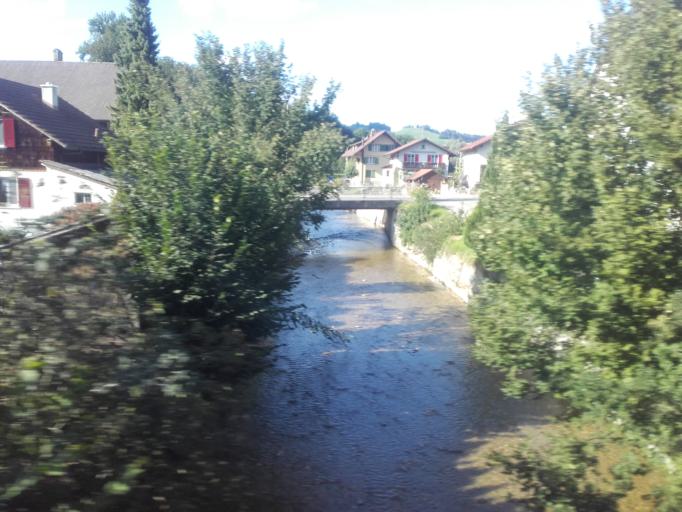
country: CH
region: Bern
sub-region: Emmental District
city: Lutzelfluh
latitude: 46.9972
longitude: 7.7052
